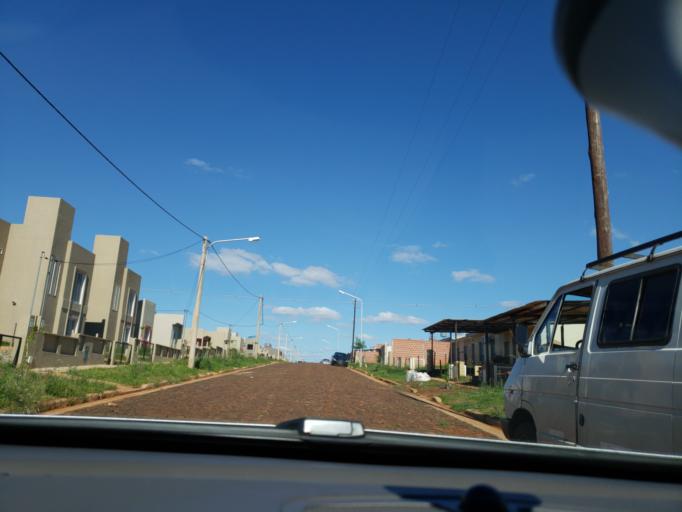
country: AR
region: Misiones
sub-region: Departamento de Capital
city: Posadas
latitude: -27.4035
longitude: -55.9863
